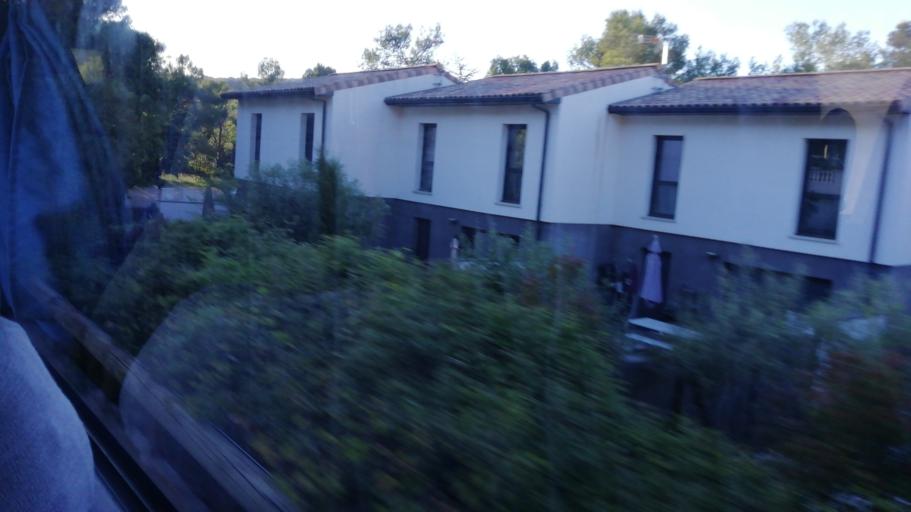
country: FR
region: Languedoc-Roussillon
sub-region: Departement de l'Herault
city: Les Matelles
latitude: 43.7298
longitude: 3.8133
